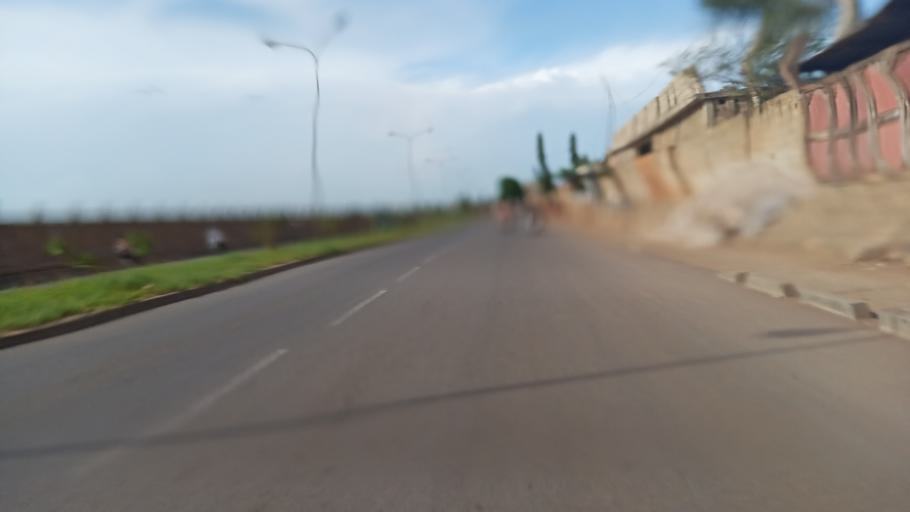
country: TG
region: Maritime
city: Lome
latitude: 6.1818
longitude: 1.2701
